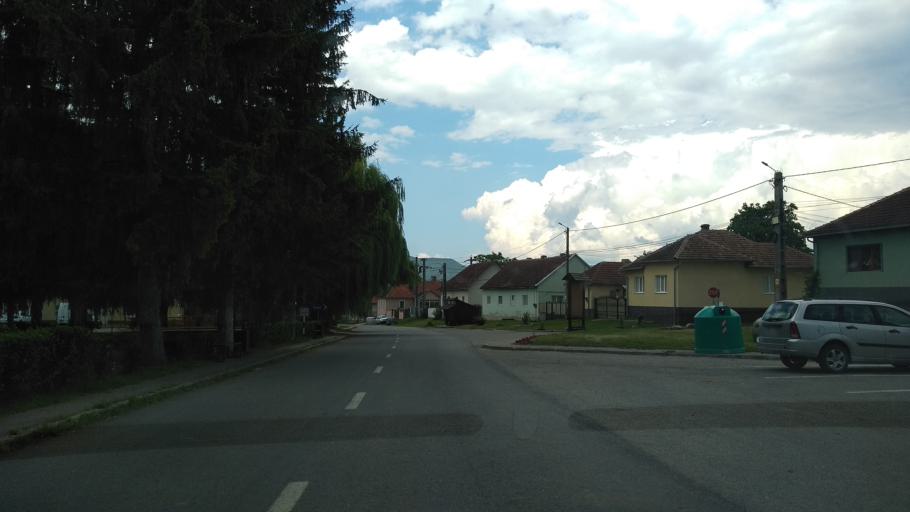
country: RO
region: Hunedoara
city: Salasu de Sus
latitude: 45.5098
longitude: 22.9545
